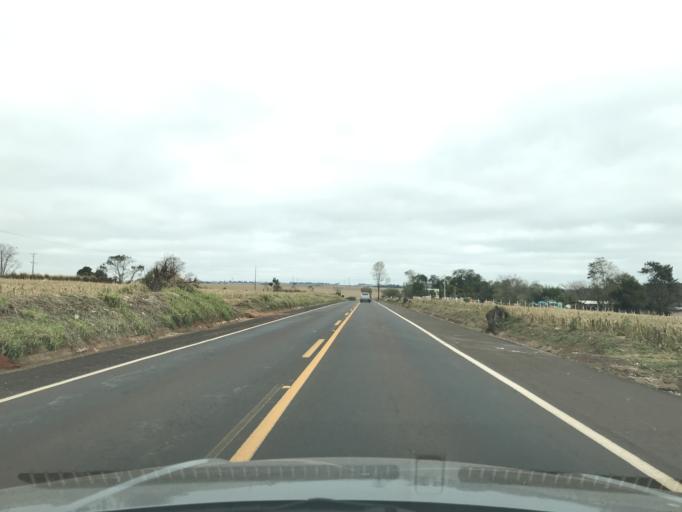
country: PY
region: Canindeyu
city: Salto del Guaira
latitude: -24.0903
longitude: -54.1919
